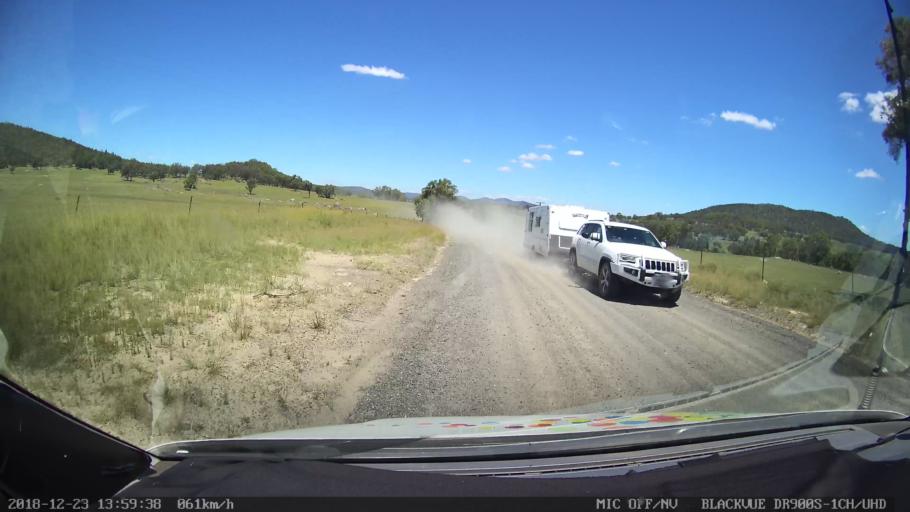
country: AU
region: New South Wales
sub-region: Tamworth Municipality
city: Manilla
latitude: -30.6097
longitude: 151.0974
